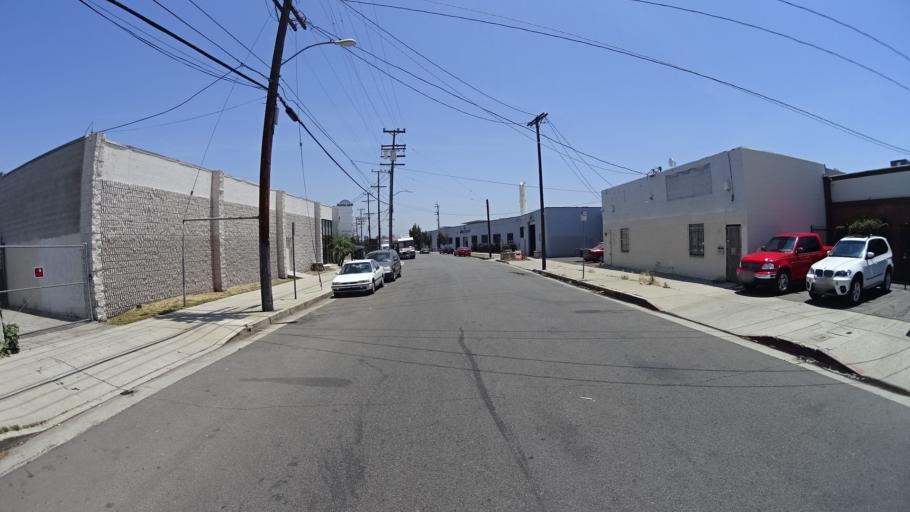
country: US
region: California
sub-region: Los Angeles County
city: Van Nuys
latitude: 34.2135
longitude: -118.4537
